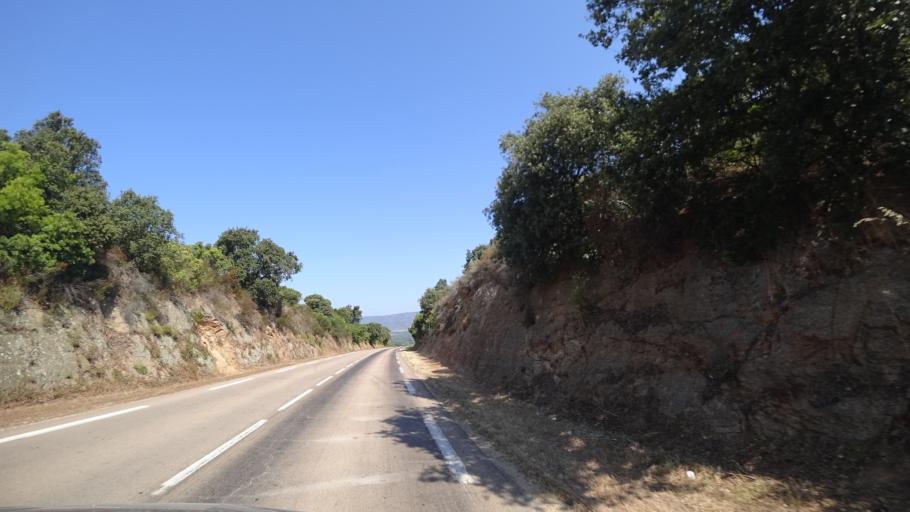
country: FR
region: Corsica
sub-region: Departement de la Corse-du-Sud
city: Bonifacio
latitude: 41.4730
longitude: 9.0917
